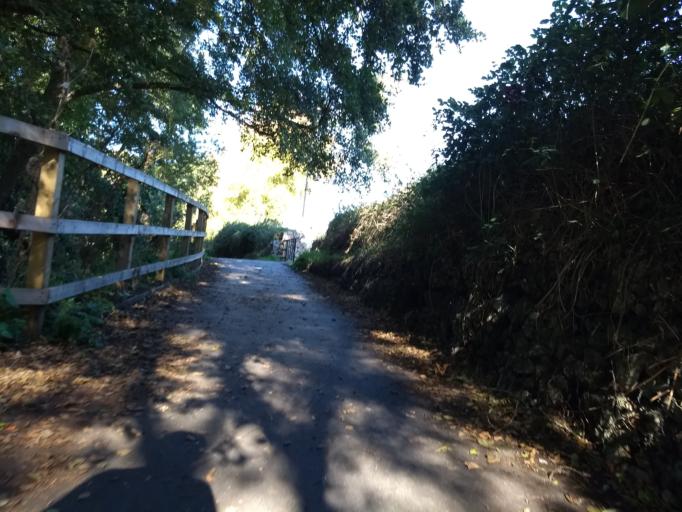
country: GB
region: England
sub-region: Isle of Wight
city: Newport
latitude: 50.6942
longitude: -1.2883
